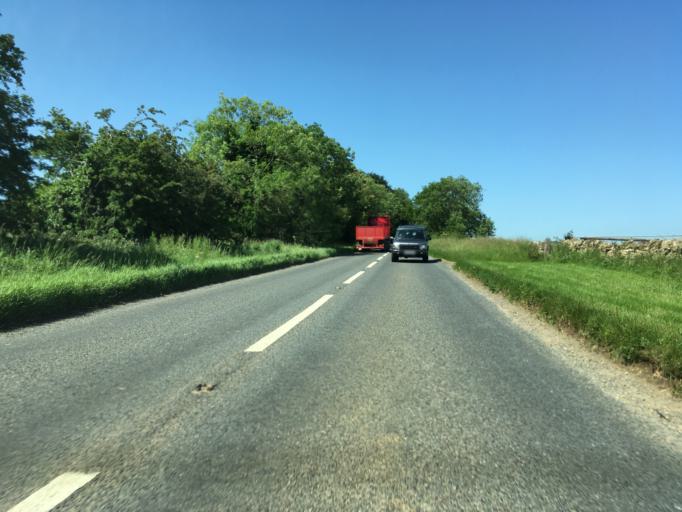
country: GB
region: England
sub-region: Gloucestershire
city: Stow on the Wold
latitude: 51.9296
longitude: -1.6875
